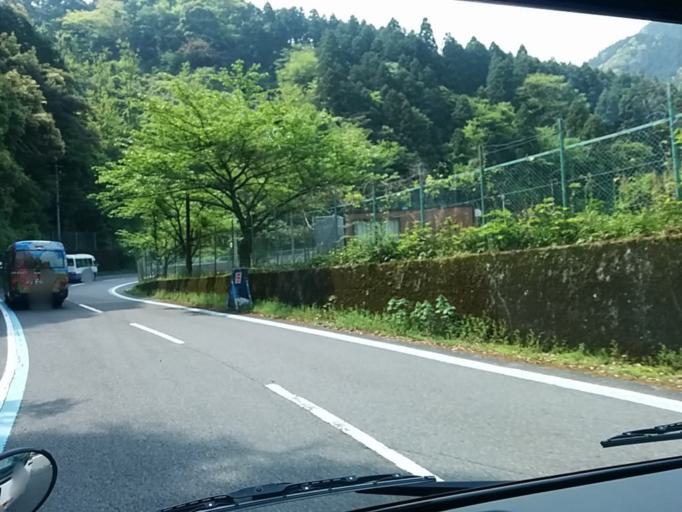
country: JP
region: Ehime
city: Niihama
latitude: 33.9004
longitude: 133.3106
